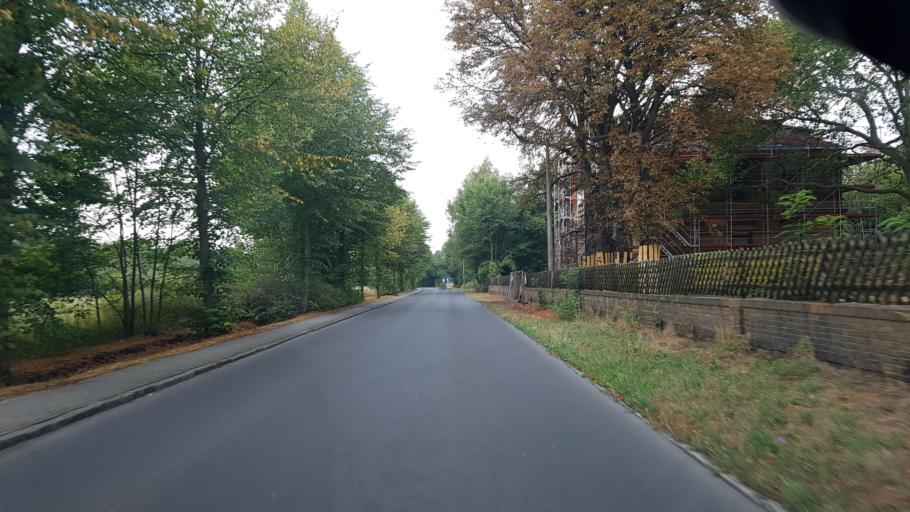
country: DE
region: Brandenburg
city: Lauchhammer
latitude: 51.4846
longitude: 13.7478
